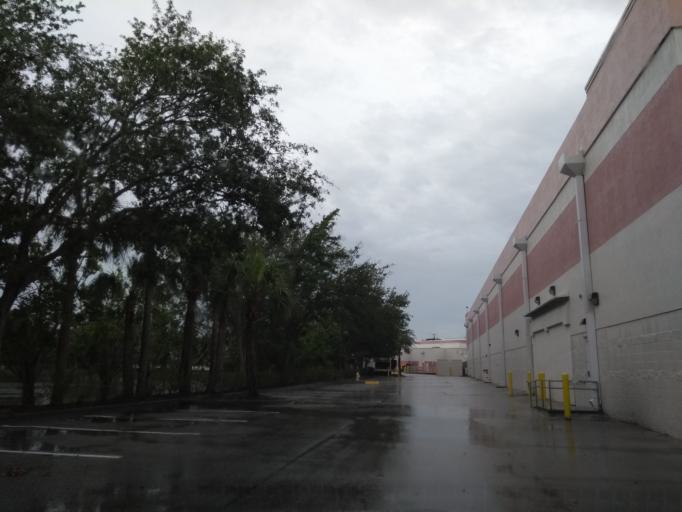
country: US
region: Florida
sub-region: Collier County
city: Pine Ridge
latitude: 26.2093
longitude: -81.7659
